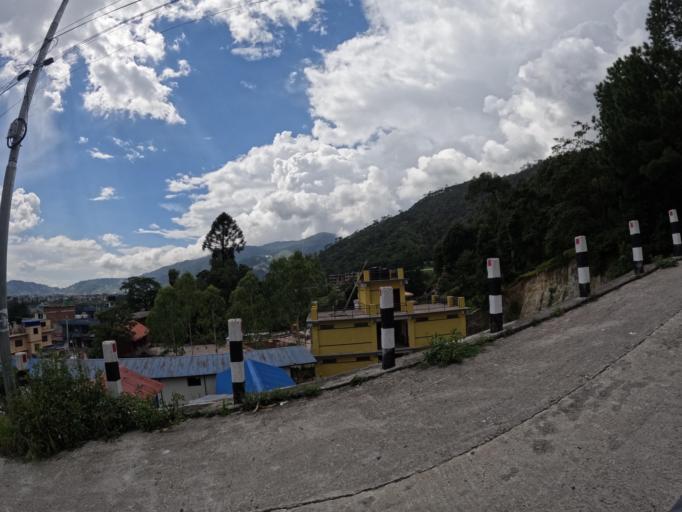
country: NP
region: Central Region
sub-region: Bagmati Zone
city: Kathmandu
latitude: 27.7770
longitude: 85.3399
